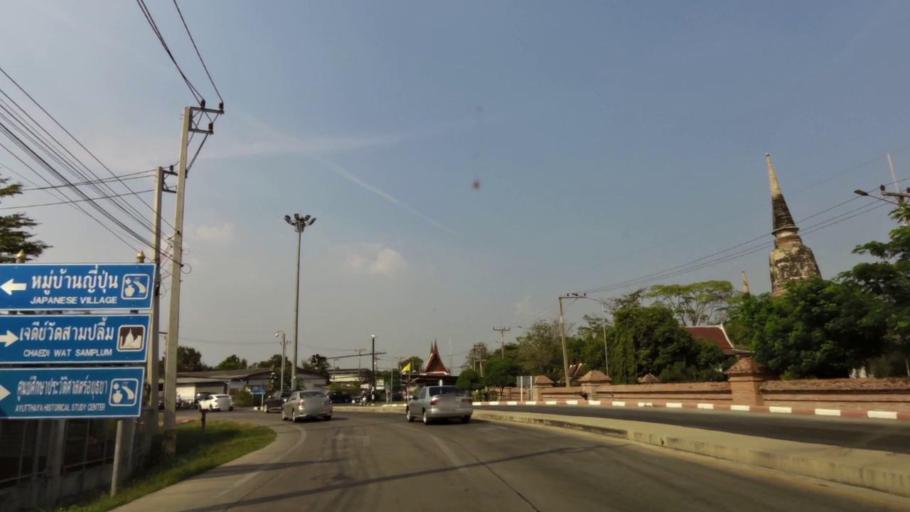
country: TH
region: Phra Nakhon Si Ayutthaya
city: Phra Nakhon Si Ayutthaya
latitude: 14.3441
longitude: 100.5916
